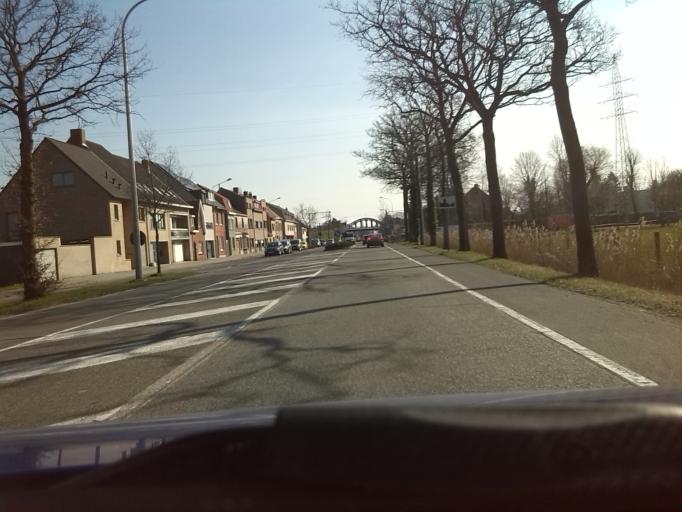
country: BE
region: Flanders
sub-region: Provincie West-Vlaanderen
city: Brugge
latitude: 51.2345
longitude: 3.2030
